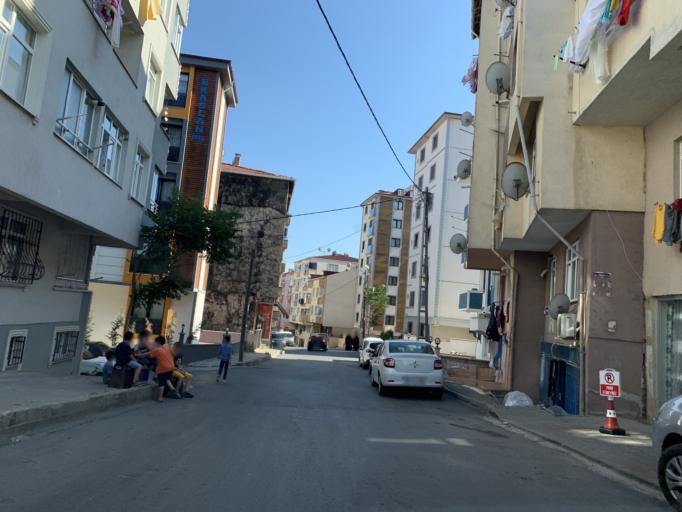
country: TR
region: Istanbul
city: Pendik
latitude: 40.8750
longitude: 29.2752
